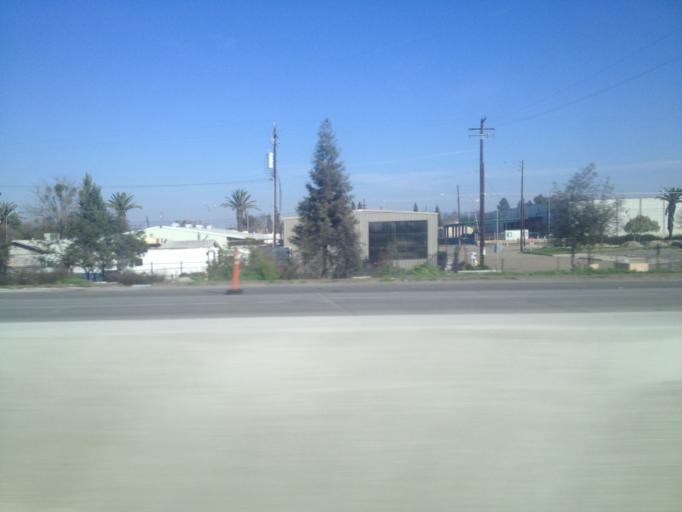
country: US
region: California
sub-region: Fresno County
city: Kingsburg
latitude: 36.5110
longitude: -119.5533
